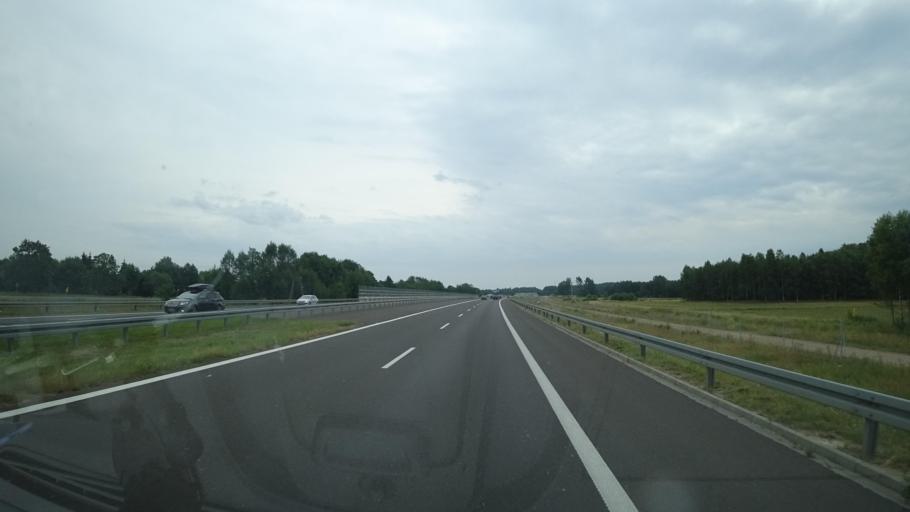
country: PL
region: Warmian-Masurian Voivodeship
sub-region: Powiat olsztynski
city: Olsztynek
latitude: 53.5877
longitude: 20.2137
